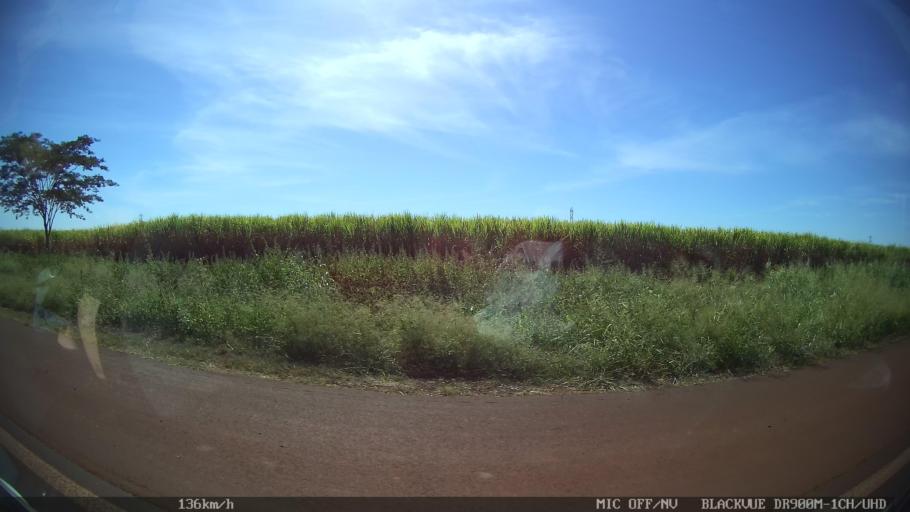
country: BR
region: Sao Paulo
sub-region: Guaira
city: Guaira
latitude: -20.4446
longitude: -48.2609
